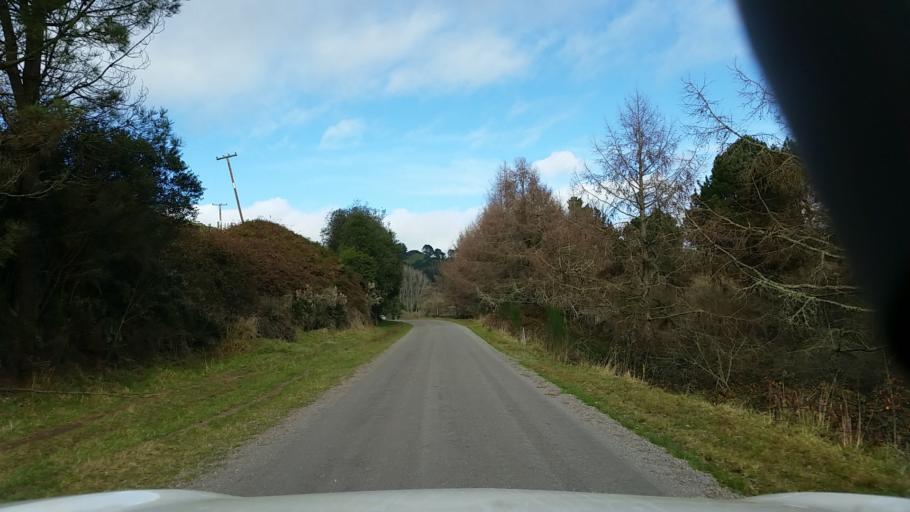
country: NZ
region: Waikato
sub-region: Taupo District
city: Taupo
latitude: -38.4593
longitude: 176.2411
